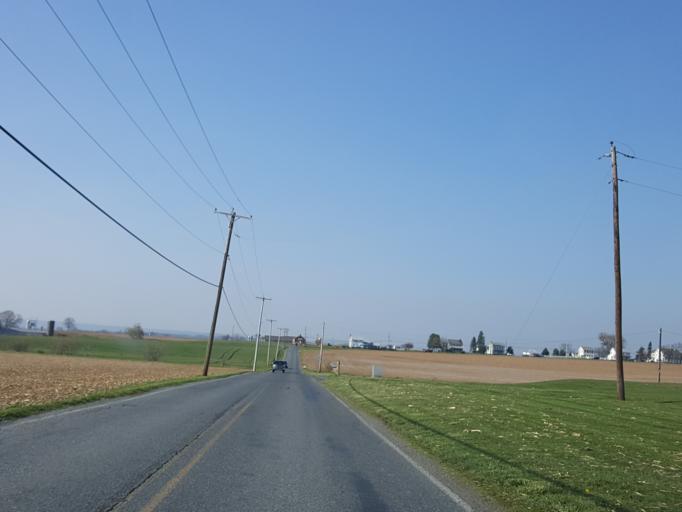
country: US
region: Pennsylvania
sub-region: Lebanon County
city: Annville
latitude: 40.2759
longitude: -76.5273
